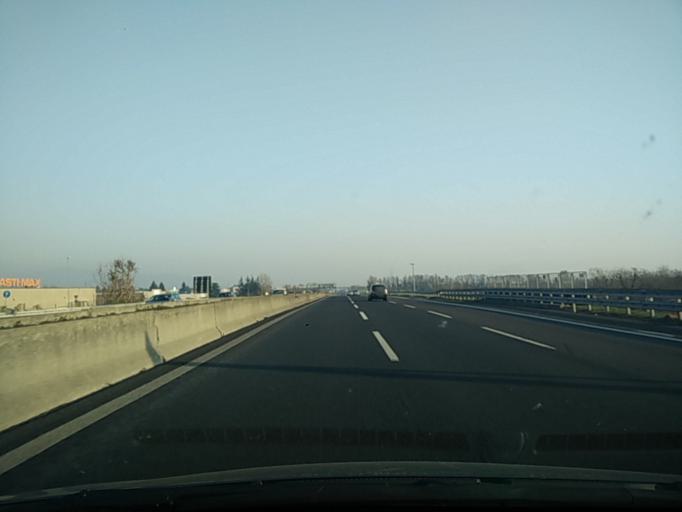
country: IT
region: Lombardy
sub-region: Provincia di Bergamo
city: Grumello del Monte
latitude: 45.6309
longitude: 9.8646
